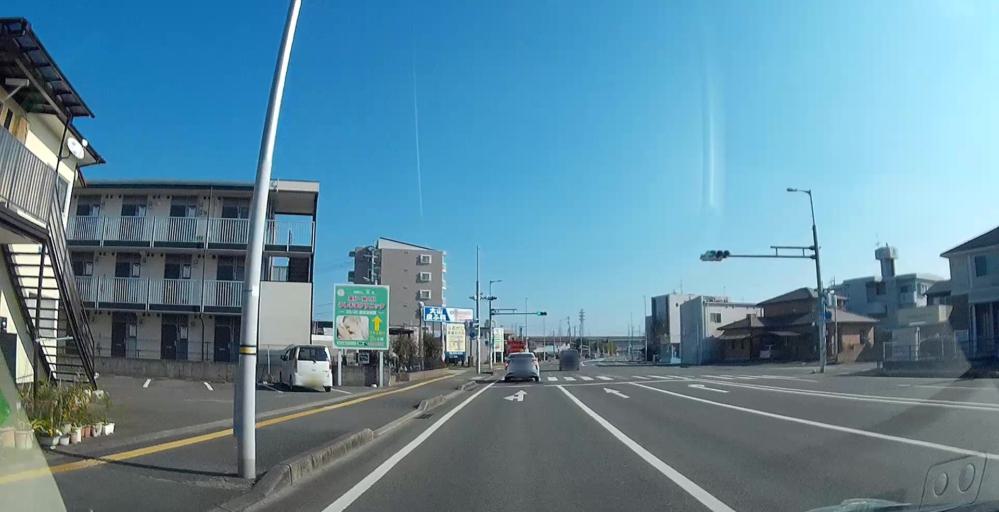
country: JP
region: Kumamoto
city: Kumamoto
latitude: 32.7753
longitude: 130.6814
